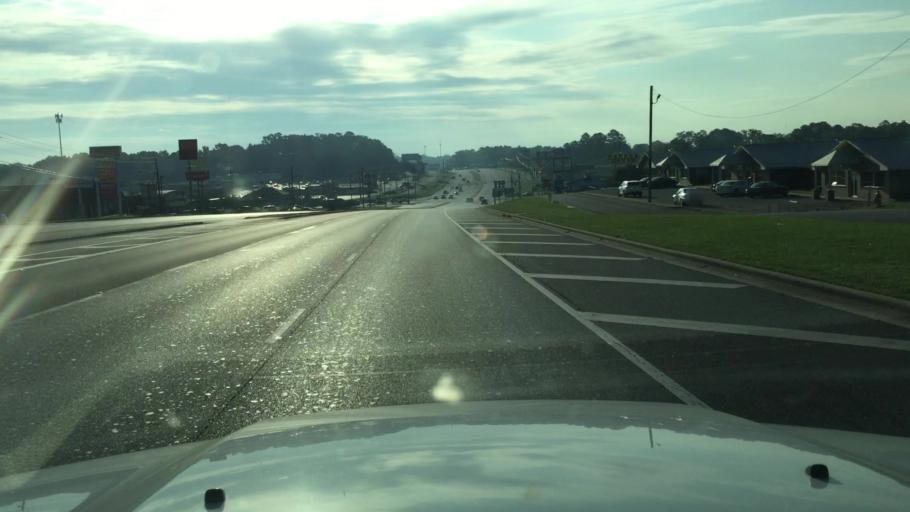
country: US
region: Alabama
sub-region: Tuscaloosa County
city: Northport
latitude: 33.2402
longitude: -87.5808
